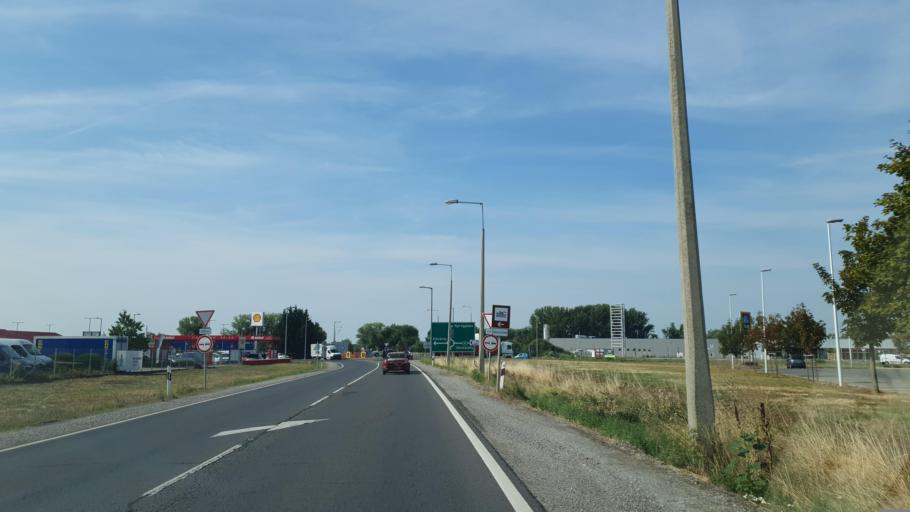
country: HU
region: Szabolcs-Szatmar-Bereg
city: Kisvarda
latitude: 48.2348
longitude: 22.0646
